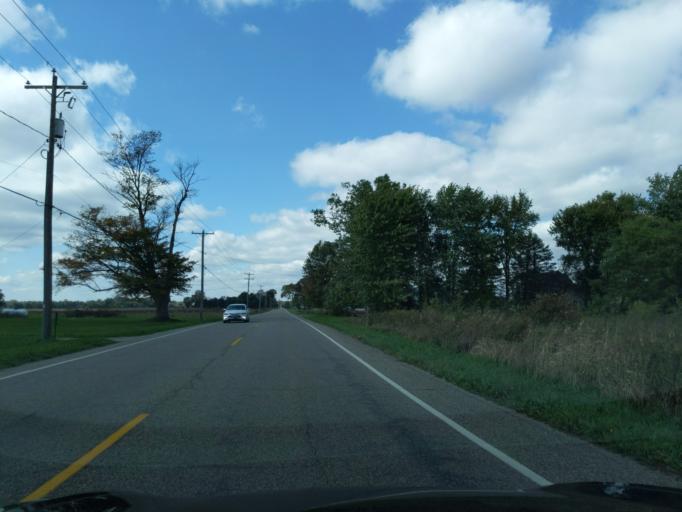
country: US
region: Michigan
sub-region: Eaton County
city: Charlotte
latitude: 42.5676
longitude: -84.8028
